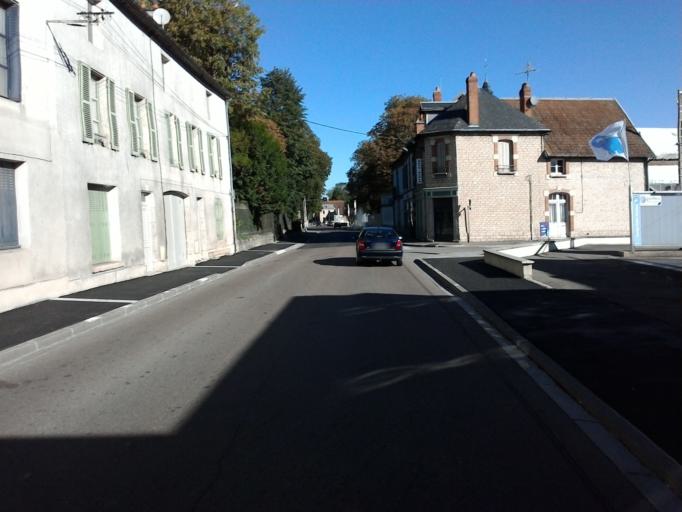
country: FR
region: Bourgogne
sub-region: Departement de la Cote-d'Or
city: Chatillon-sur-Seine
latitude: 47.8623
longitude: 4.5748
